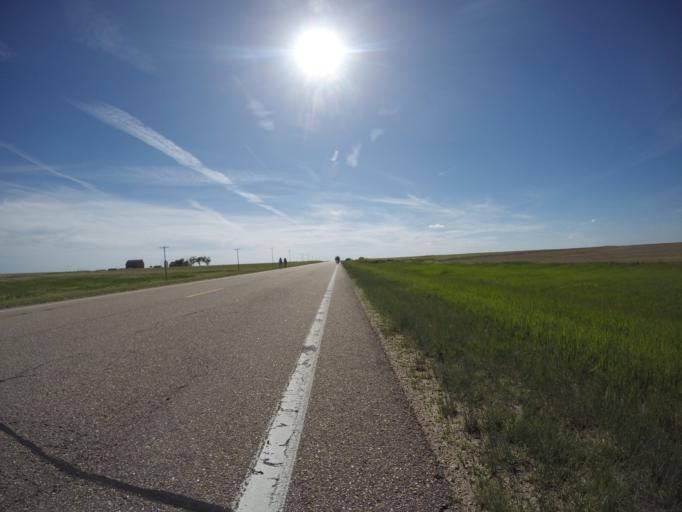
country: US
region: Kansas
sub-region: Cheyenne County
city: Saint Francis
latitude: 39.7566
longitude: -101.9828
